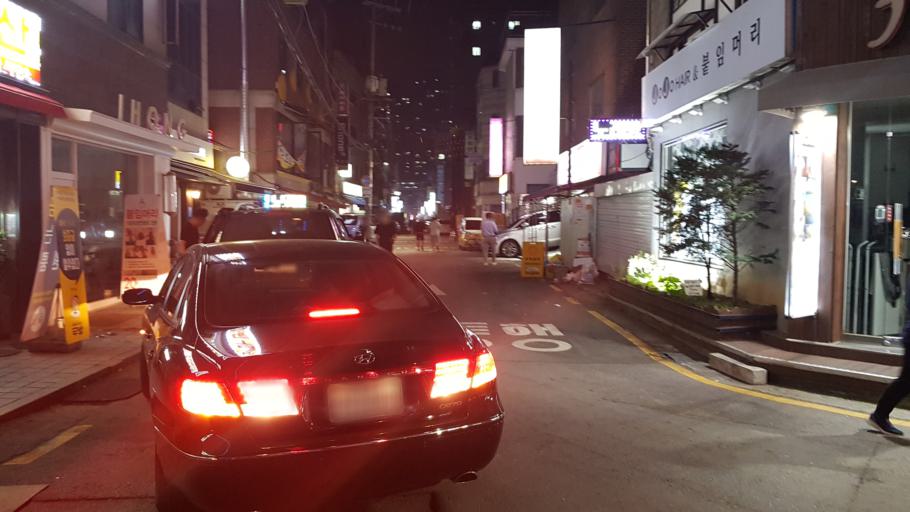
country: KR
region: Gyeonggi-do
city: Kwangmyong
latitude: 37.4847
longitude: 126.9269
